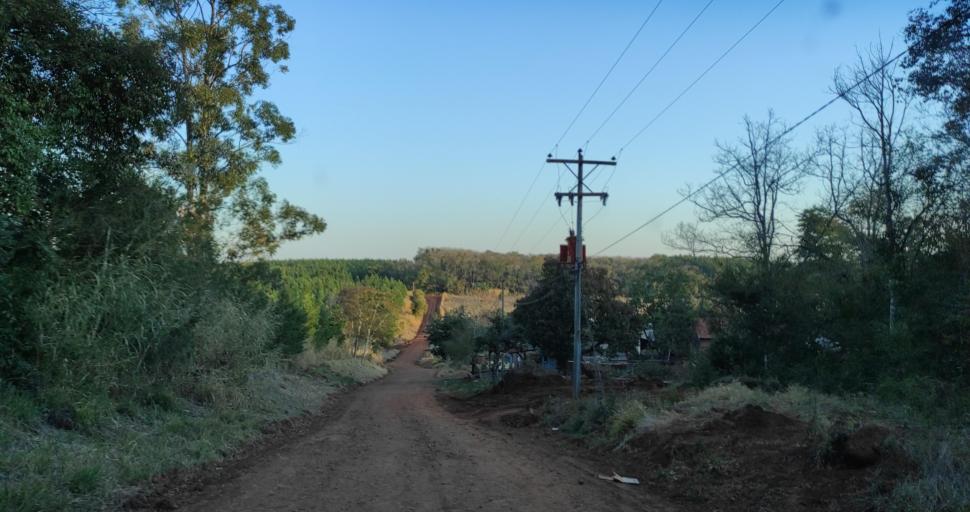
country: AR
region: Misiones
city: Capiovi
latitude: -26.8773
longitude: -55.1229
